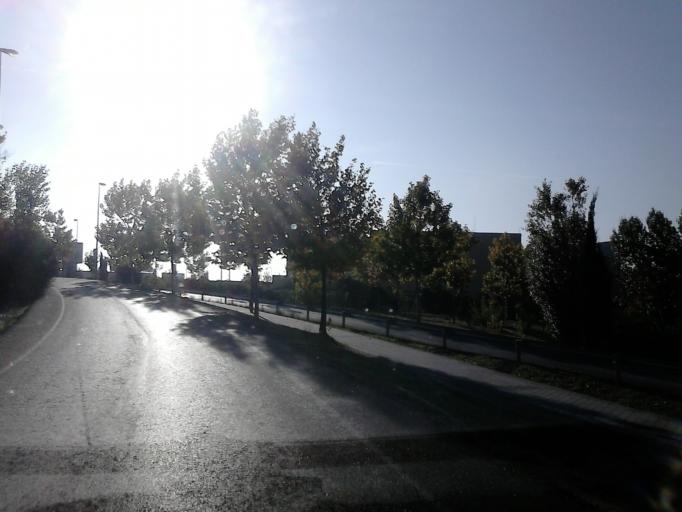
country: ES
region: Madrid
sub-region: Provincia de Madrid
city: Majadahonda
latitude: 40.4565
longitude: -3.8757
